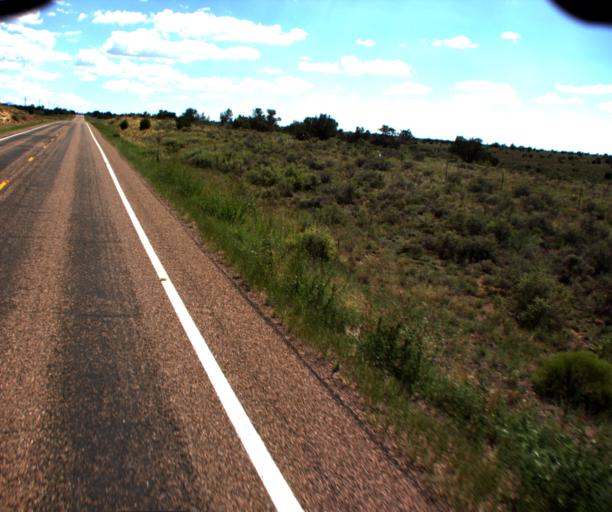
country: US
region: Arizona
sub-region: Coconino County
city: Williams
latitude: 35.5644
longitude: -112.1567
